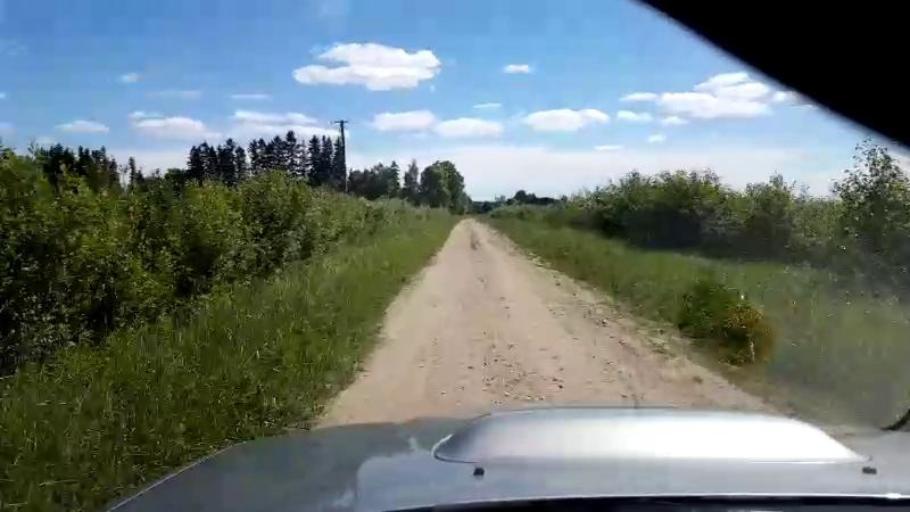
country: EE
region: Paernumaa
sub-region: Halinga vald
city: Parnu-Jaagupi
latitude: 58.5429
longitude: 24.5308
